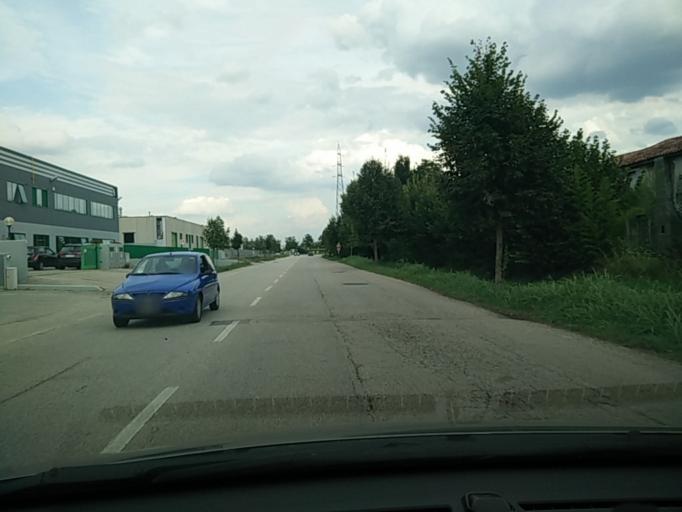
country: IT
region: Veneto
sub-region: Provincia di Treviso
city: Salvatronda
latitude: 45.6785
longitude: 11.9649
